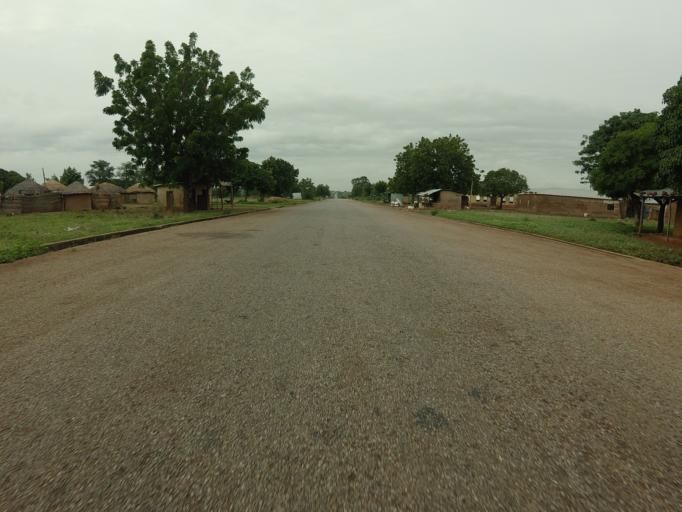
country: GH
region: Northern
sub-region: Yendi
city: Yendi
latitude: 9.5037
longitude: -0.0264
